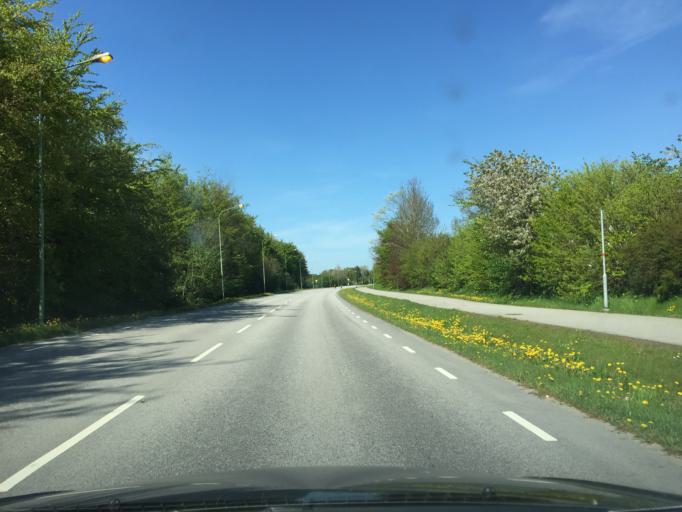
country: SE
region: Skane
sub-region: Skurups Kommun
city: Skurup
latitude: 55.4858
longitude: 13.5035
